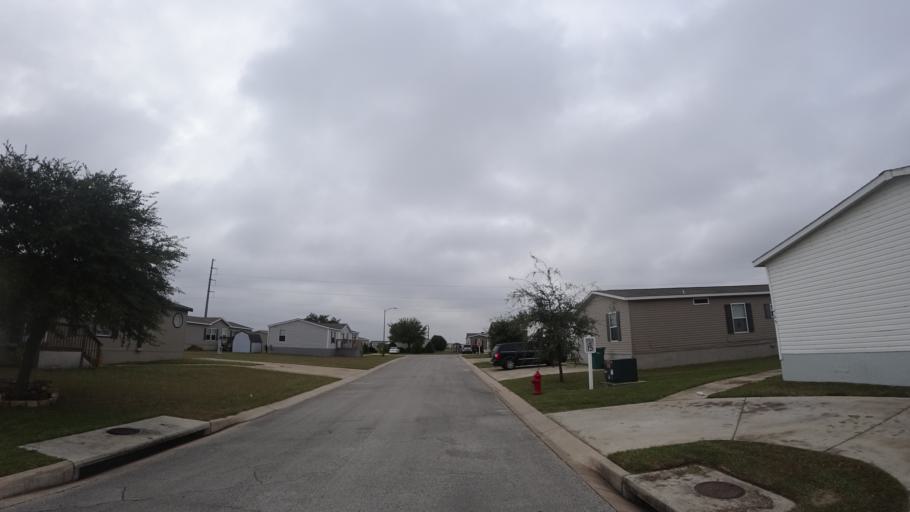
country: US
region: Texas
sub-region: Travis County
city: Pflugerville
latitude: 30.4099
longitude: -97.6070
